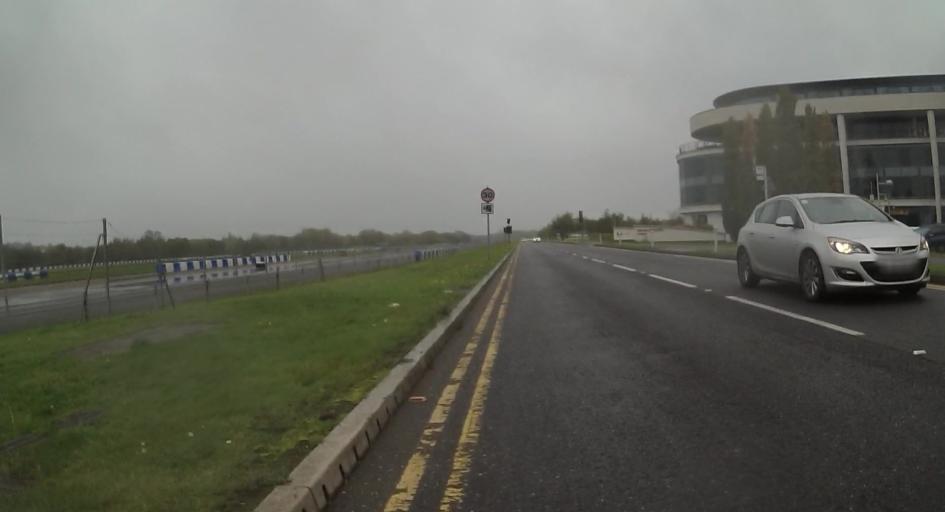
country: GB
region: England
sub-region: Surrey
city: Byfleet
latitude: 51.3529
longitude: -0.4698
